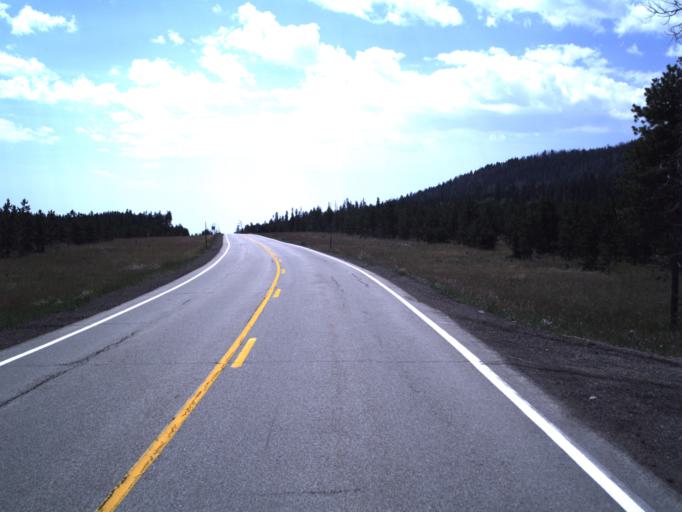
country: US
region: Utah
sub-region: Uintah County
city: Maeser
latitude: 40.7483
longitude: -109.4724
